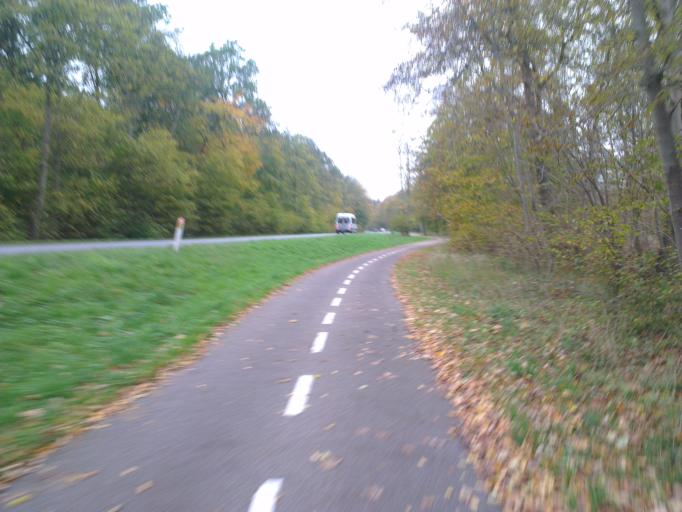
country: DK
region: Capital Region
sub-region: Frederikssund Kommune
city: Frederikssund
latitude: 55.8443
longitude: 12.0294
